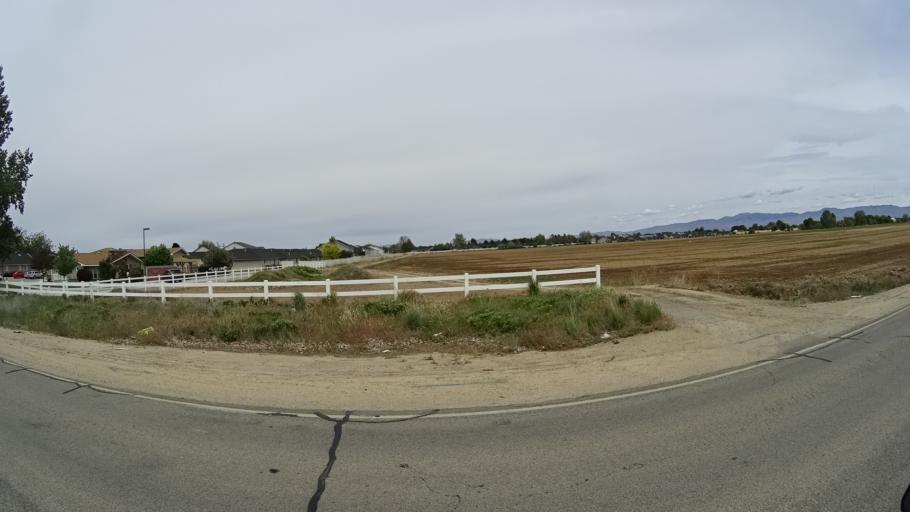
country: US
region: Idaho
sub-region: Ada County
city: Meridian
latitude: 43.5609
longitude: -116.3490
